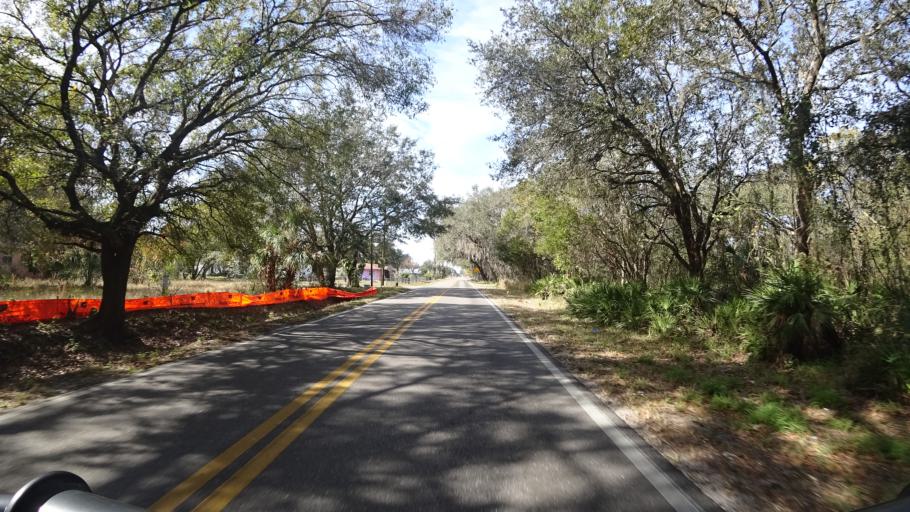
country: US
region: Florida
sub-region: Manatee County
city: Ellenton
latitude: 27.5869
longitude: -82.4299
